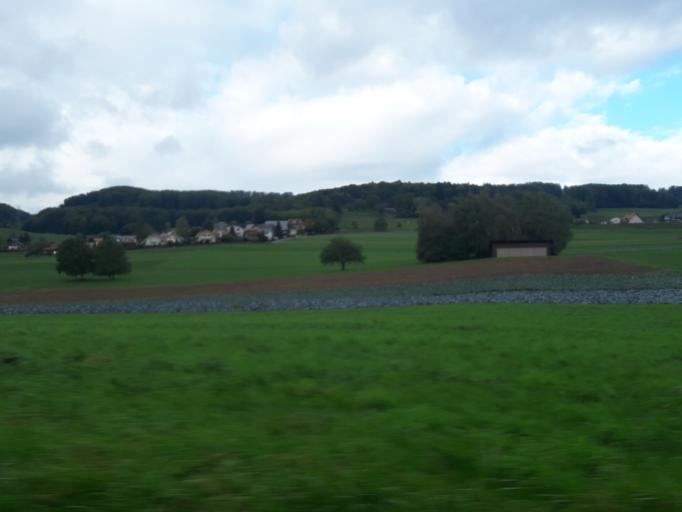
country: CH
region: Bern
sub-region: Bern-Mittelland District
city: Muhlethurnen
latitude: 46.8206
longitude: 7.5119
